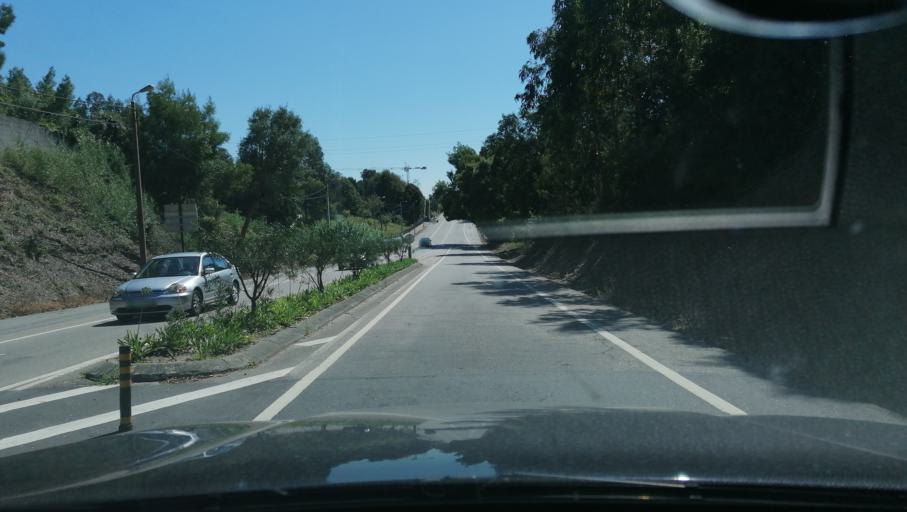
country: PT
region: Porto
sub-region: Vila Nova de Gaia
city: Gulpilhares
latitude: 41.0825
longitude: -8.6349
